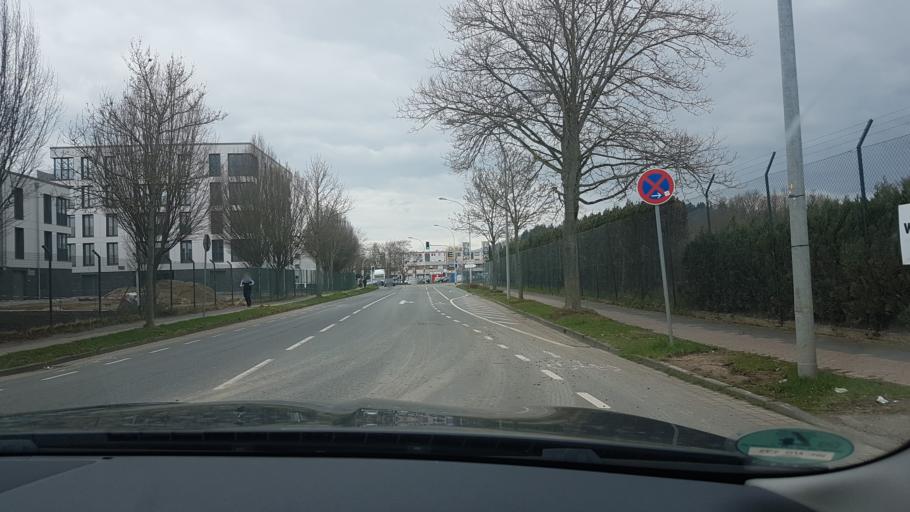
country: DE
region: Lower Saxony
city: Hameln
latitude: 52.1218
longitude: 9.3485
